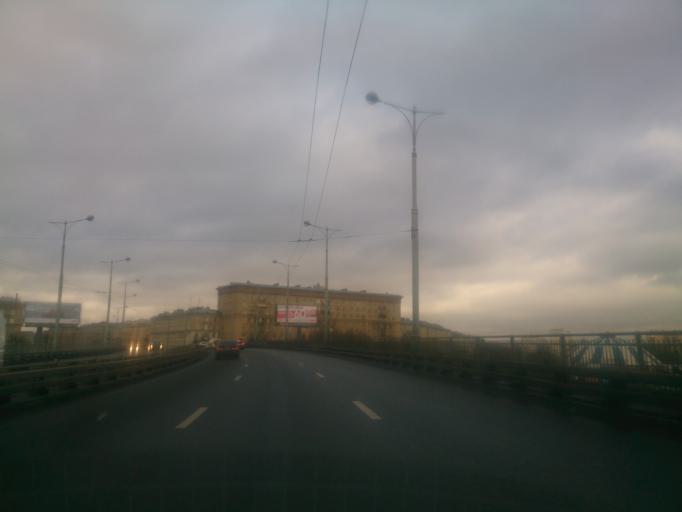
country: RU
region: St.-Petersburg
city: Avtovo
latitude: 59.8633
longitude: 30.2608
